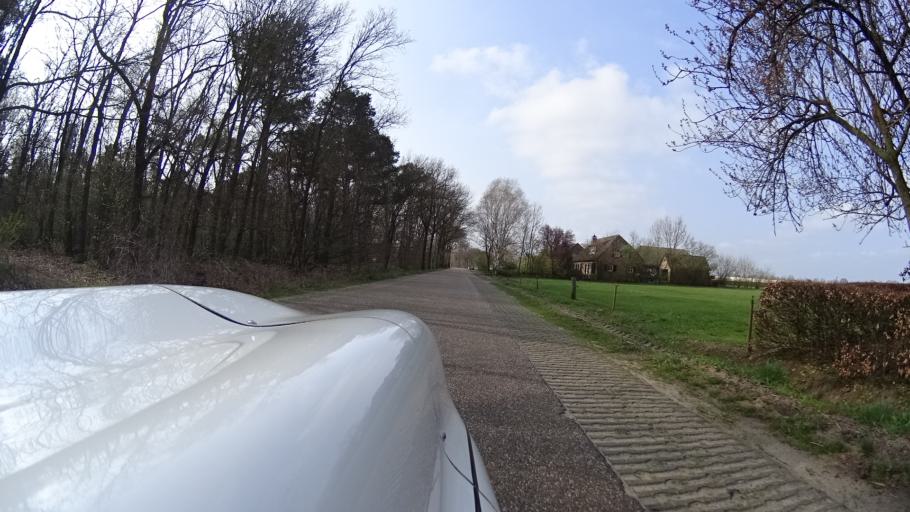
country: NL
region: North Brabant
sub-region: Gemeente Helmond
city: Helmond
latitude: 51.5310
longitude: 5.7009
